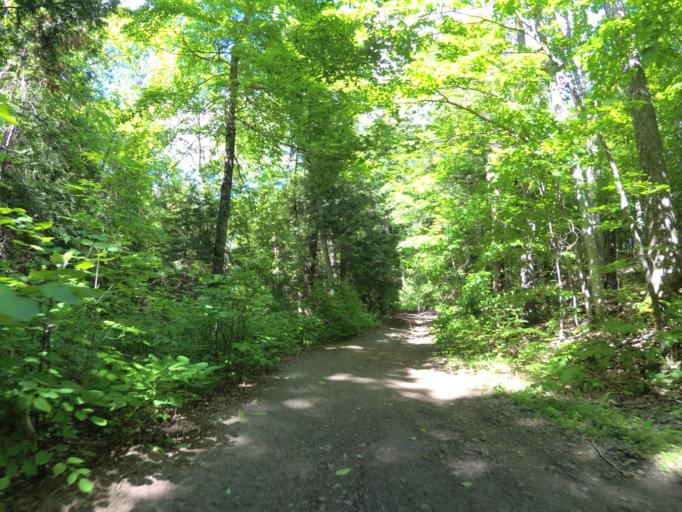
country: CA
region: Ontario
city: Renfrew
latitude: 45.0440
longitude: -76.8368
